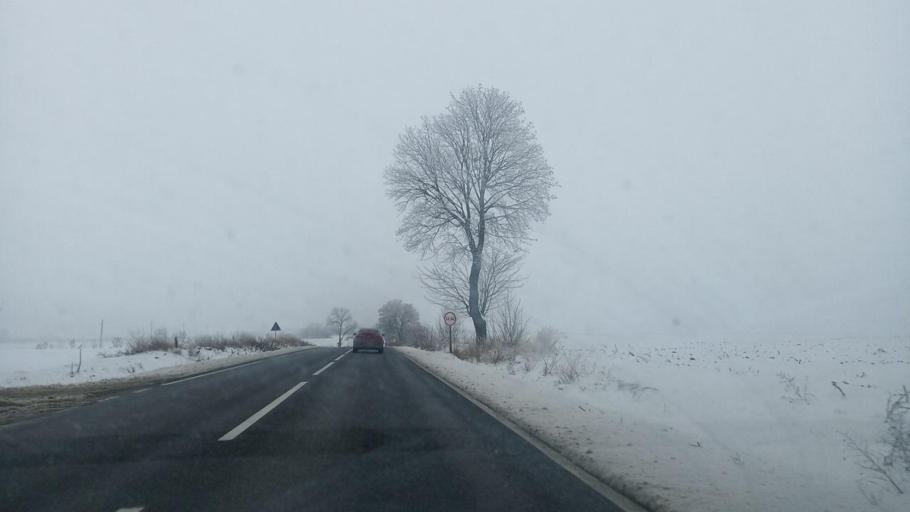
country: RO
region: Neamt
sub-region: Comuna Botesti
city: Nisiporesti
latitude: 47.0926
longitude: 26.7071
